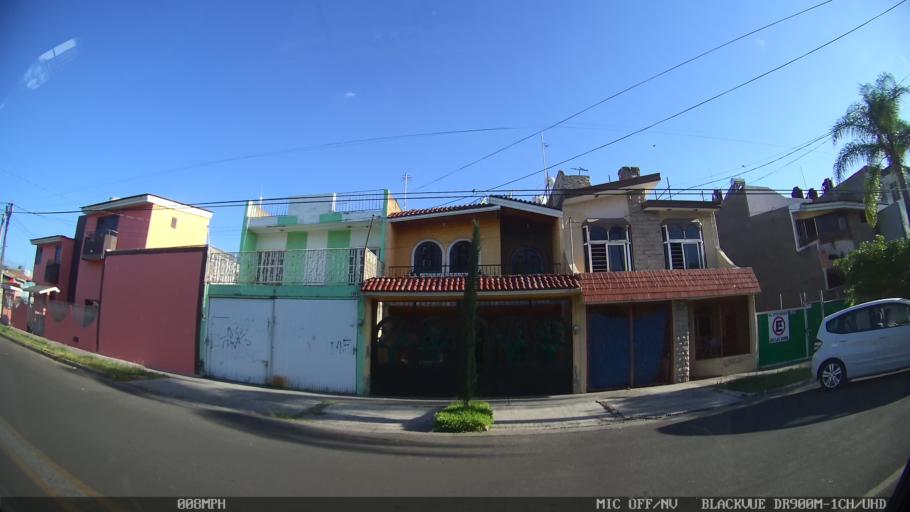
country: MX
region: Jalisco
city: Tlaquepaque
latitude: 20.7011
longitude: -103.2968
